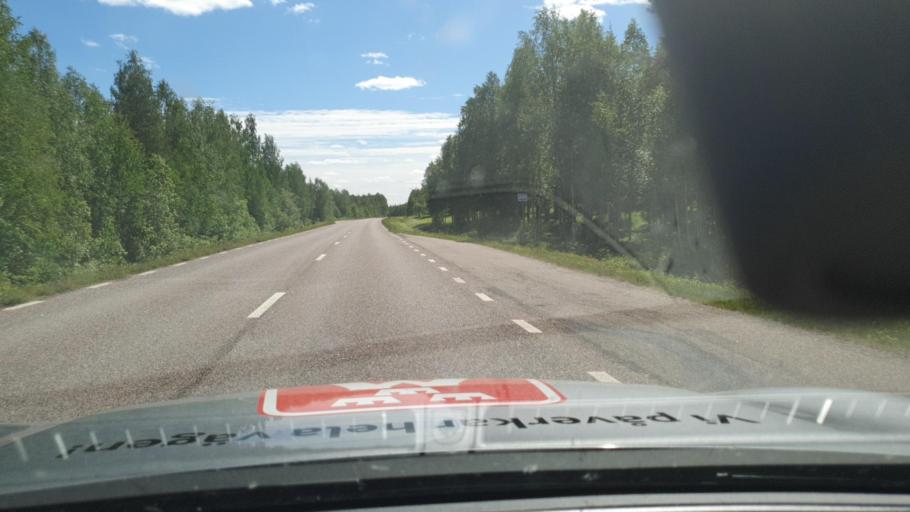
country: FI
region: Lapland
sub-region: Tunturi-Lappi
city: Kolari
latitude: 67.0560
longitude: 23.6766
